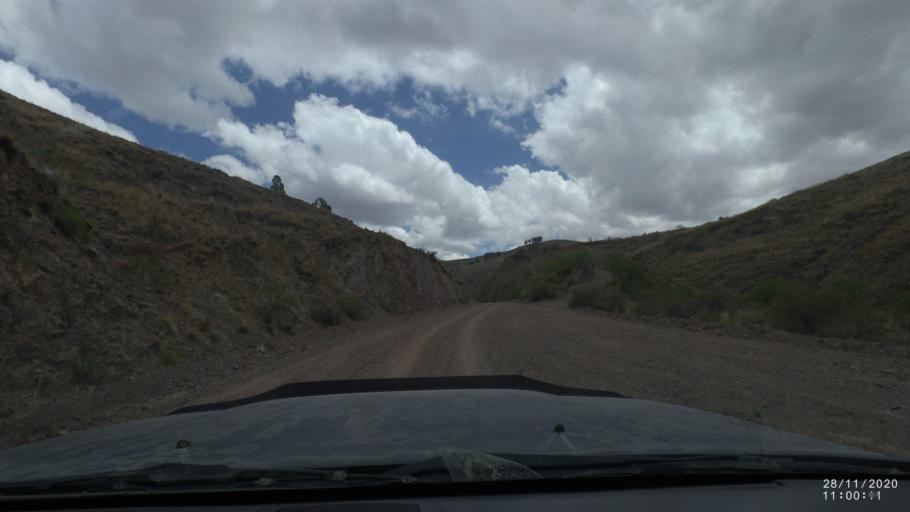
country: BO
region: Cochabamba
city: Capinota
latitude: -17.7704
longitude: -66.1072
